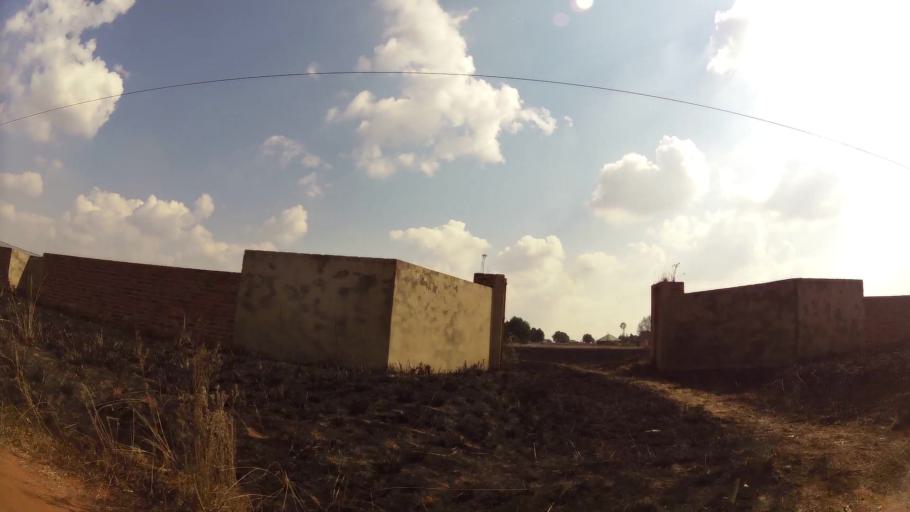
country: ZA
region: Mpumalanga
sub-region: Nkangala District Municipality
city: Delmas
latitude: -26.1704
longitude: 28.5459
